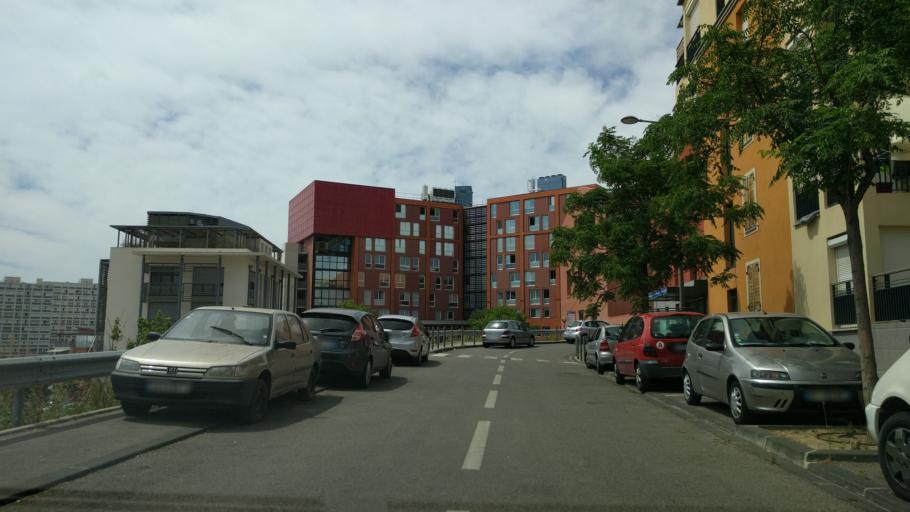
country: FR
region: Provence-Alpes-Cote d'Azur
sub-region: Departement des Bouches-du-Rhone
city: Marseille 13
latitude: 43.3335
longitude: 5.4020
